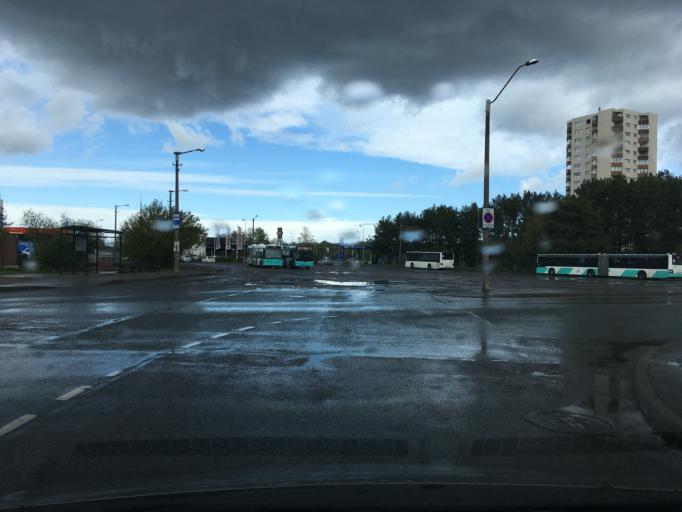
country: EE
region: Harju
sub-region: Tallinna linn
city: Kose
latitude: 59.4446
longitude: 24.8967
